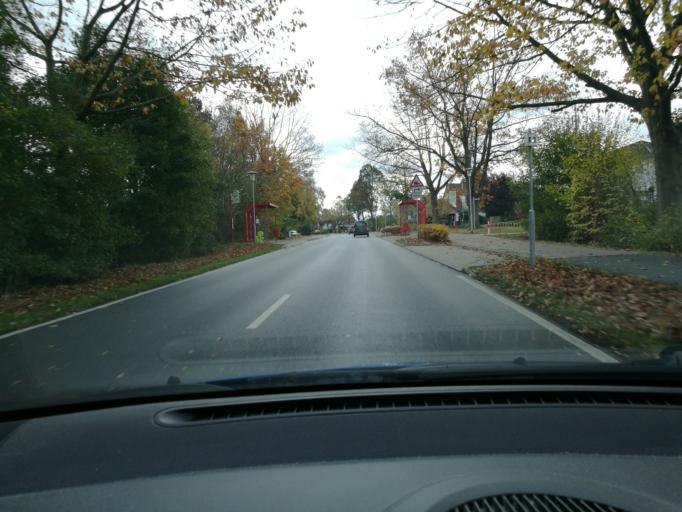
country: DE
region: Schleswig-Holstein
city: Pogeez
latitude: 53.7550
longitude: 10.7291
